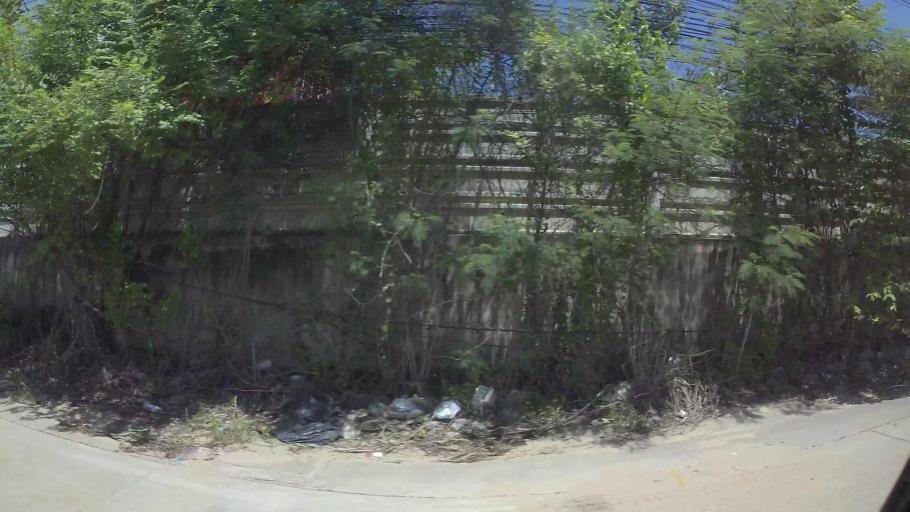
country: TH
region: Chon Buri
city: Si Racha
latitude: 13.1174
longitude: 100.9572
